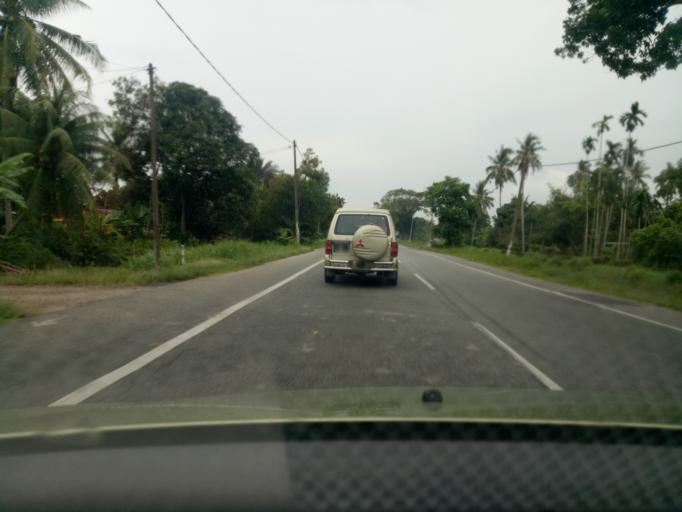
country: MY
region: Kedah
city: Gurun
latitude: 5.8919
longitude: 100.4406
